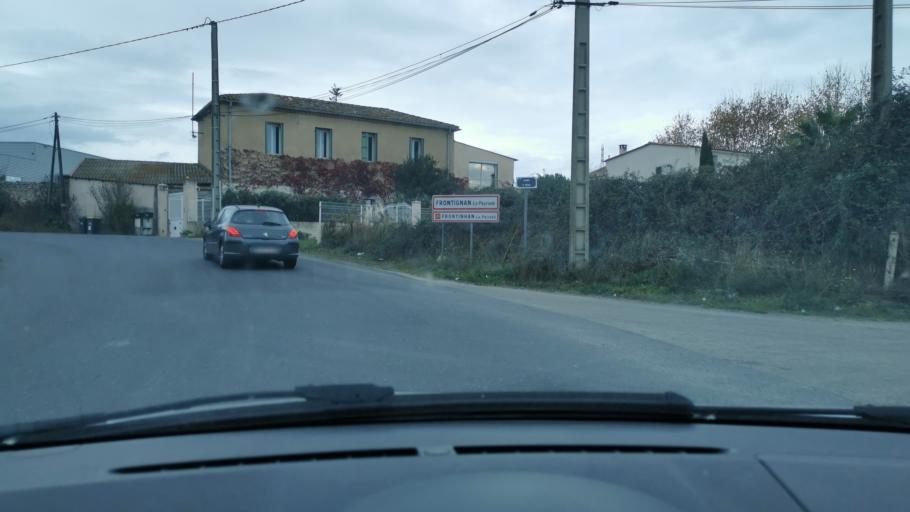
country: FR
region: Languedoc-Roussillon
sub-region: Departement de l'Herault
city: Balaruc-les-Bains
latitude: 43.4336
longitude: 3.7028
